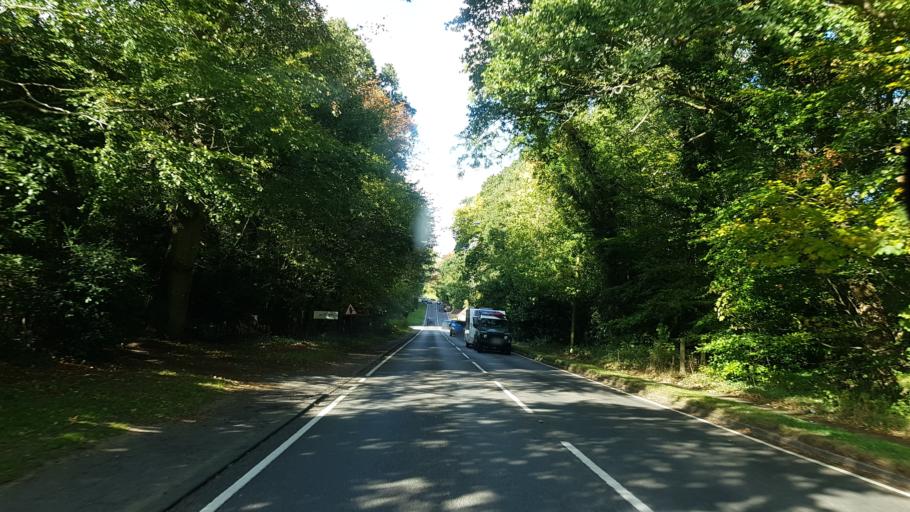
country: GB
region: England
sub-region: Surrey
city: Milford
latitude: 51.1416
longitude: -0.6457
